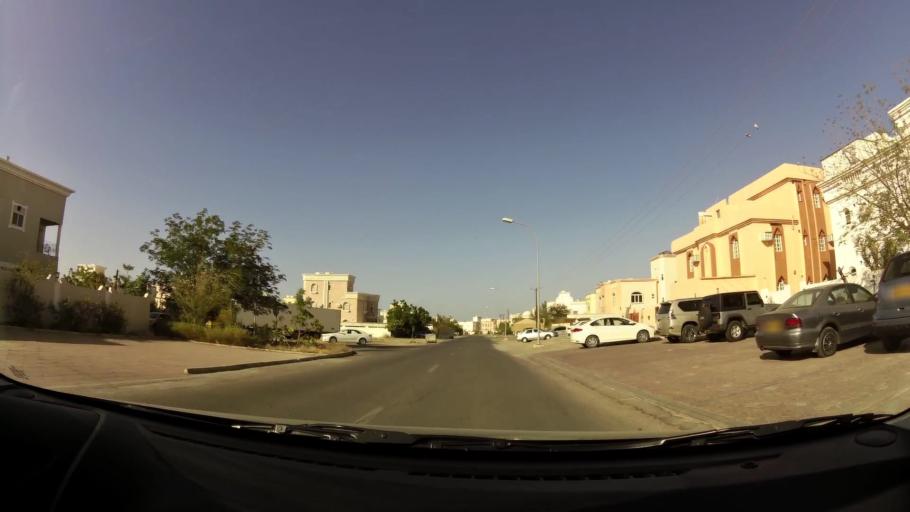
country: OM
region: Muhafazat Masqat
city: As Sib al Jadidah
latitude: 23.5981
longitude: 58.2130
